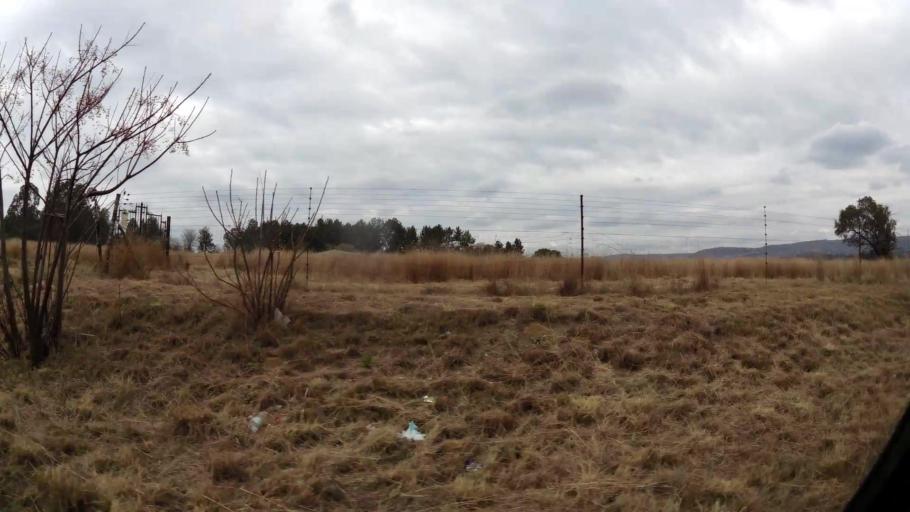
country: ZA
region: Gauteng
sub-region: West Rand District Municipality
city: Muldersdriseloop
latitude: -26.0548
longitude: 27.8878
